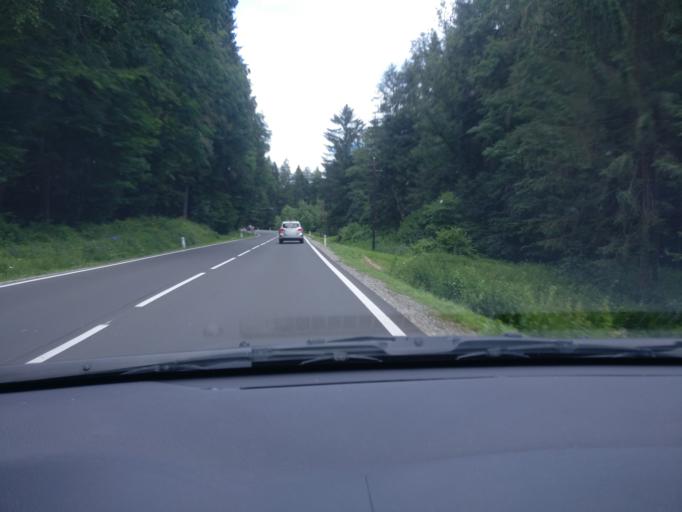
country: AT
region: Styria
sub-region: Politischer Bezirk Weiz
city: Oberrettenbach
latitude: 47.1572
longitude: 15.7735
